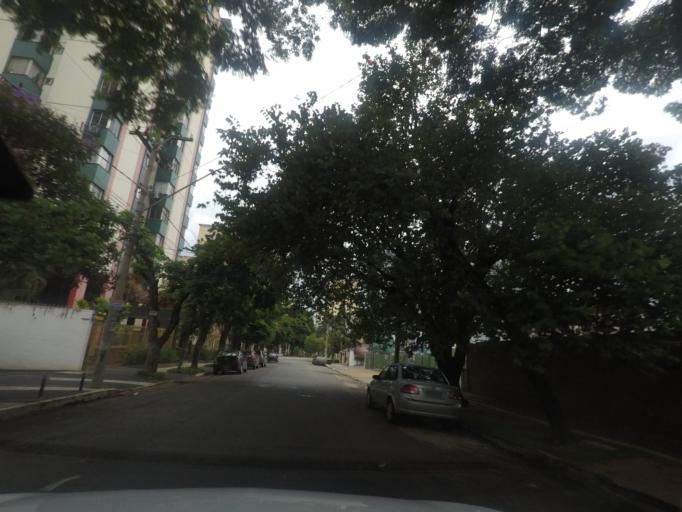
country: BR
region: Goias
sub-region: Goiania
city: Goiania
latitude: -16.6834
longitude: -49.2670
